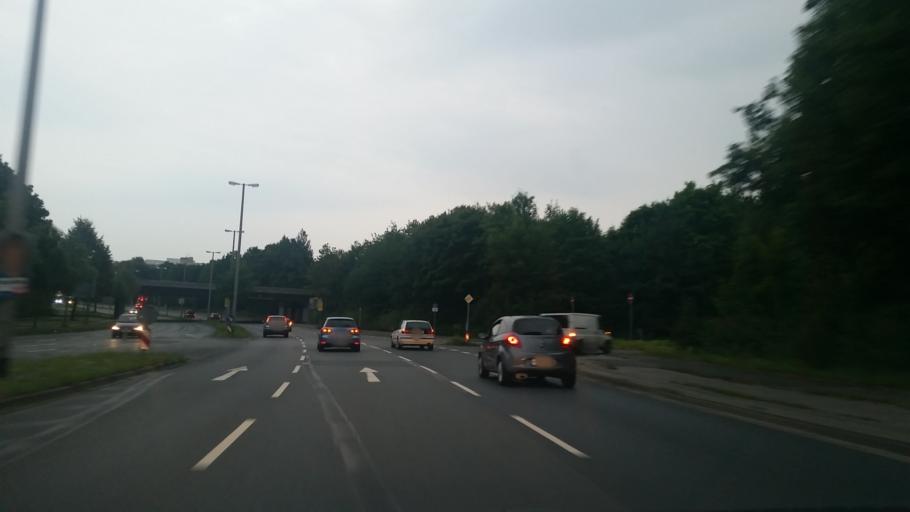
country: DE
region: Lower Saxony
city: Ronnenberg
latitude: 52.3490
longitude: 9.6894
